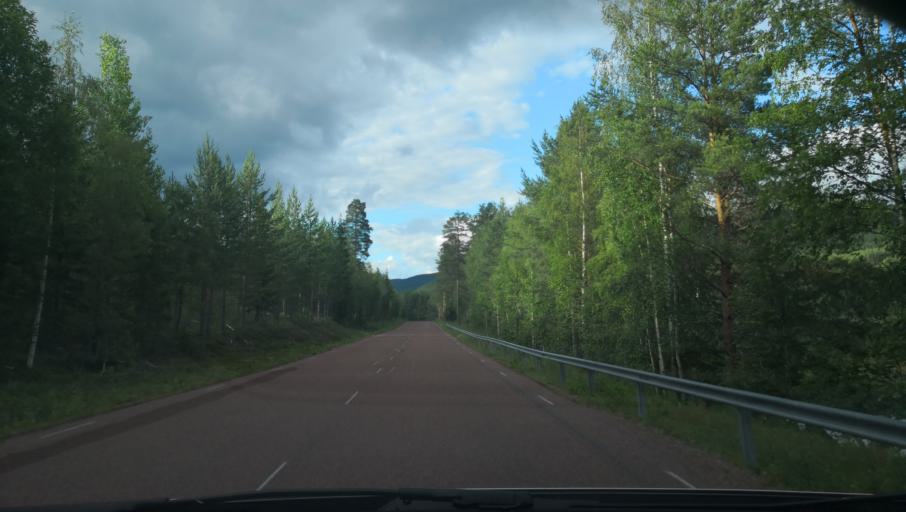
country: SE
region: Dalarna
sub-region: Alvdalens Kommun
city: AElvdalen
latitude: 61.3123
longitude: 13.7301
